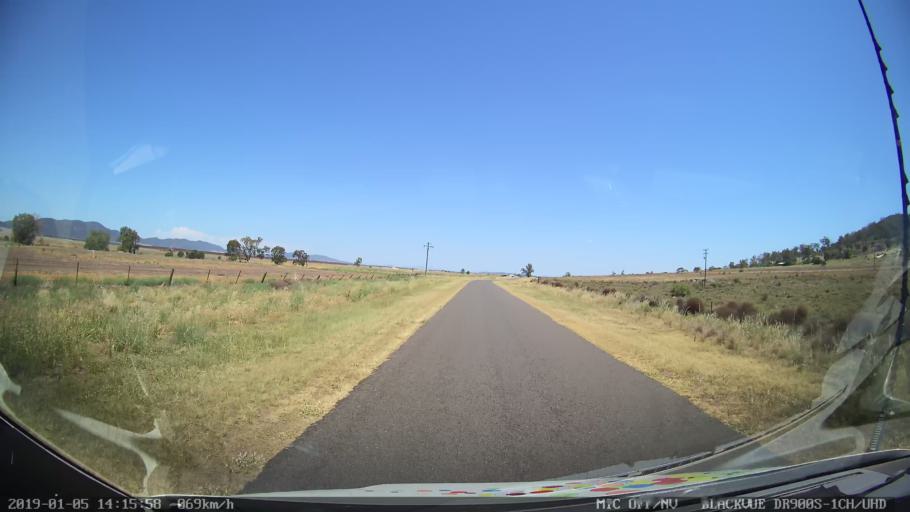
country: AU
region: New South Wales
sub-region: Liverpool Plains
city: Quirindi
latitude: -31.2521
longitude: 150.4720
